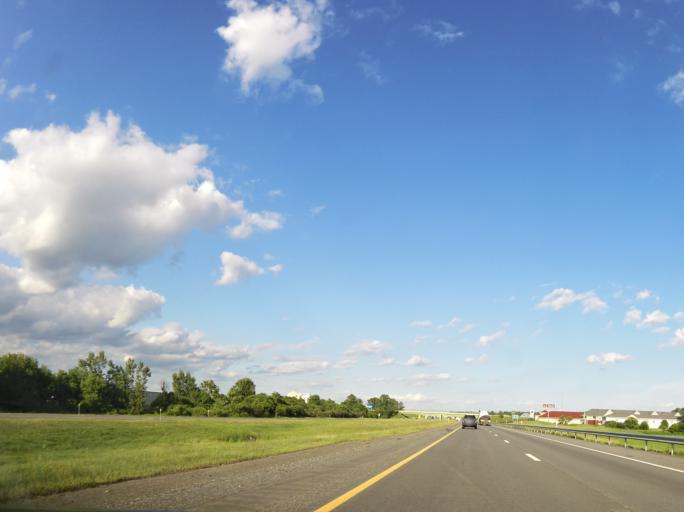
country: US
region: New York
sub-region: Genesee County
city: Batavia
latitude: 43.0179
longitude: -78.1988
